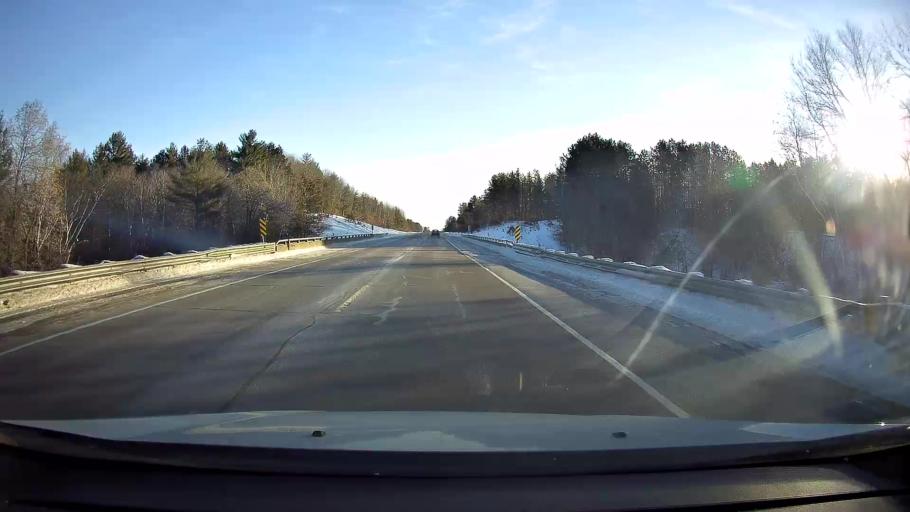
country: US
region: Wisconsin
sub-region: Washburn County
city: Spooner
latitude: 45.9104
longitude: -91.7819
